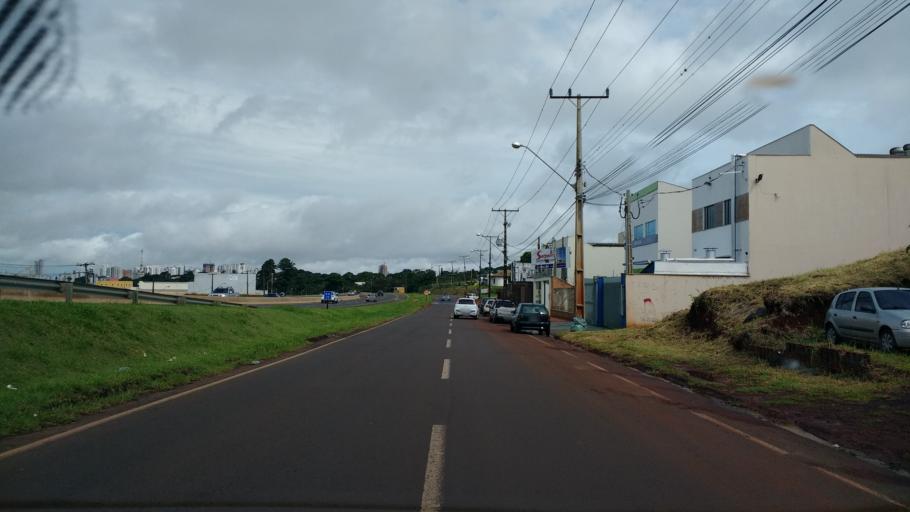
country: BR
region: Parana
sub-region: Londrina
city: Londrina
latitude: -23.3184
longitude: -51.2100
